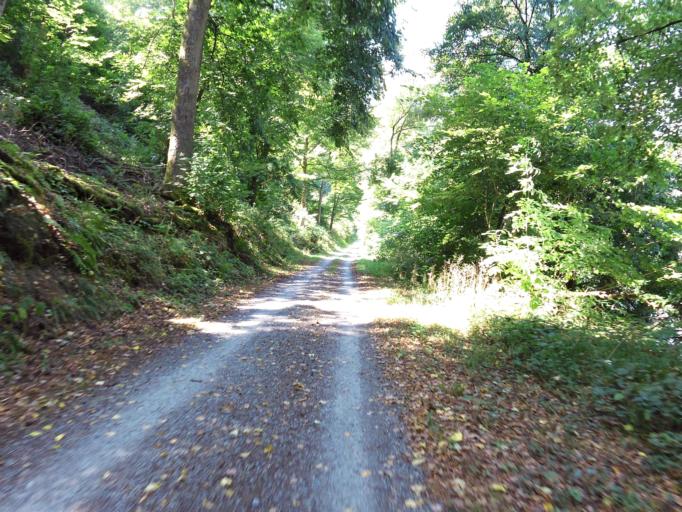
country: DE
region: Baden-Wuerttemberg
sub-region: Karlsruhe Region
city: Neunkirchen
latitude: 49.4145
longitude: 9.0073
